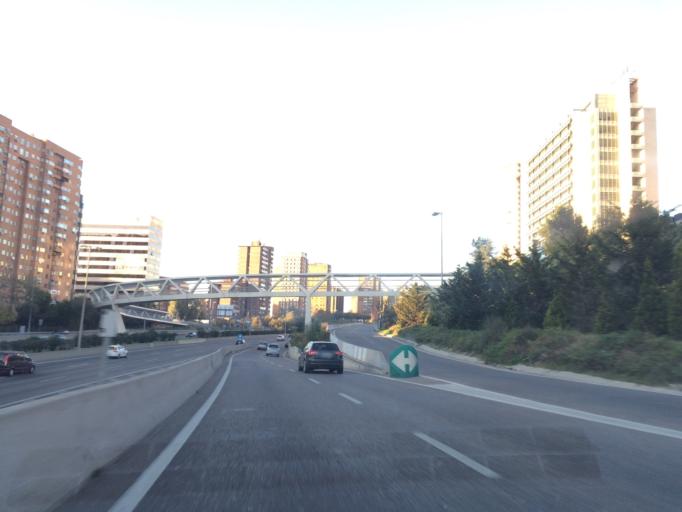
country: ES
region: Madrid
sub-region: Provincia de Madrid
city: Pinar de Chamartin
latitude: 40.4740
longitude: -3.6733
